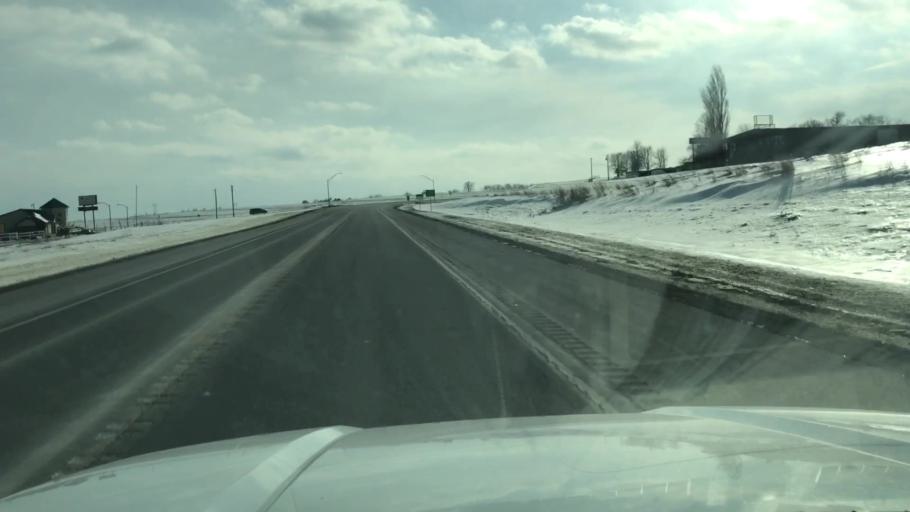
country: US
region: Missouri
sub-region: Nodaway County
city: Maryville
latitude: 40.3366
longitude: -94.8538
